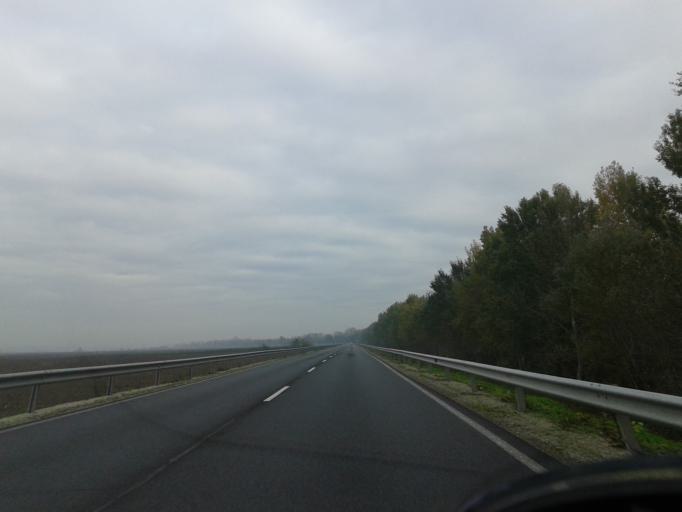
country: HU
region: Fejer
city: Ercsi
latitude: 47.2026
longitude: 18.8764
